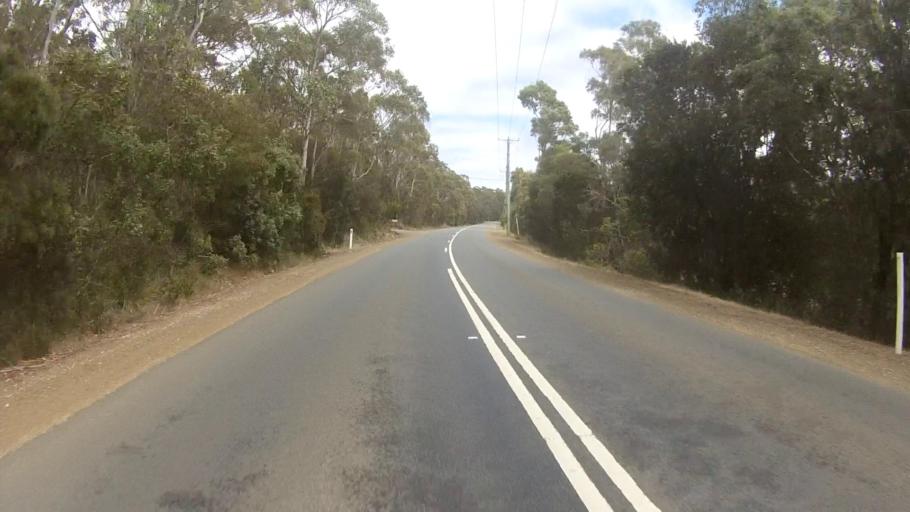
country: AU
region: Tasmania
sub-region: Kingborough
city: Margate
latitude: -43.0057
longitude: 147.2405
